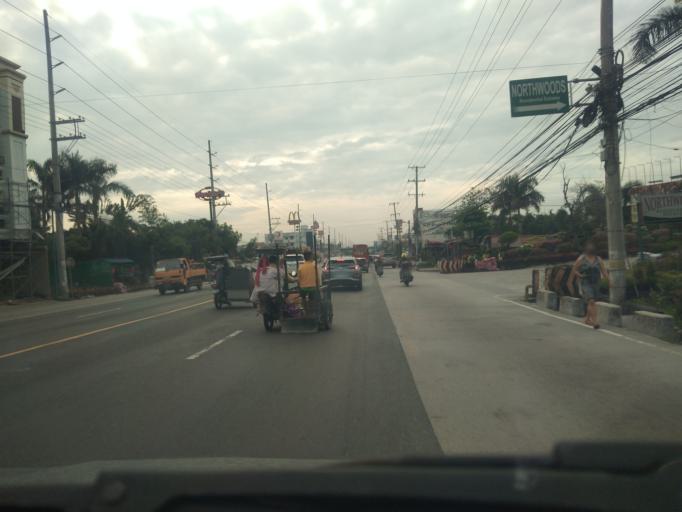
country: PH
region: Central Luzon
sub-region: Province of Pampanga
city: Bulaon
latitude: 15.0666
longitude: 120.6504
